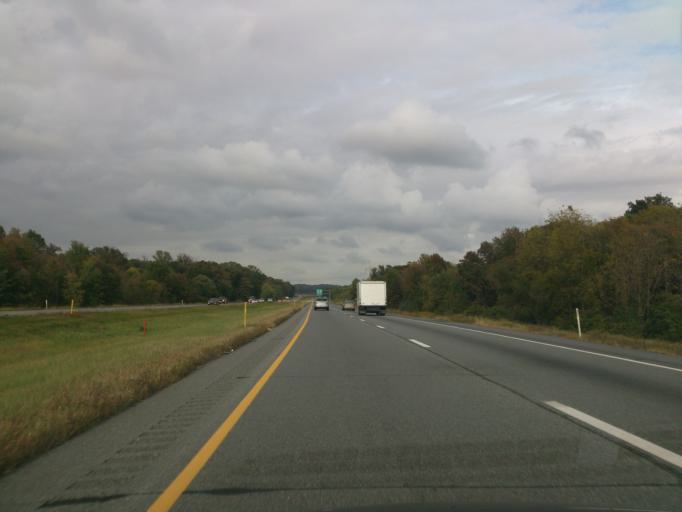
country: US
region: Pennsylvania
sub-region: Lancaster County
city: Adamstown
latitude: 40.2300
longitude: -76.0517
